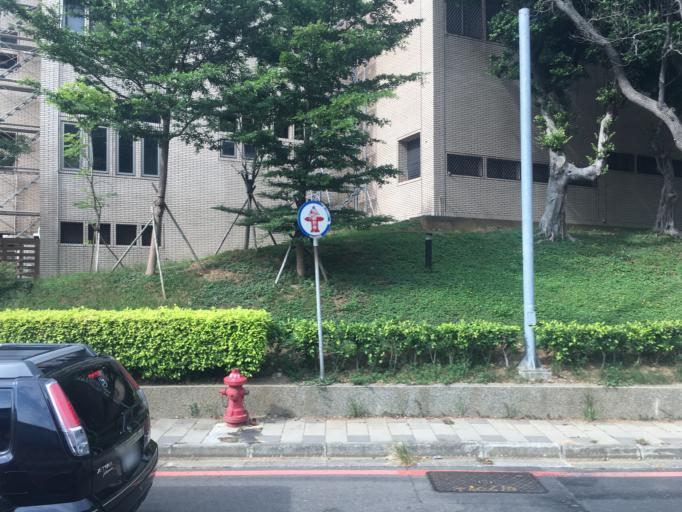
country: TW
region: Taiwan
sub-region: Hsinchu
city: Hsinchu
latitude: 24.7830
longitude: 120.9968
